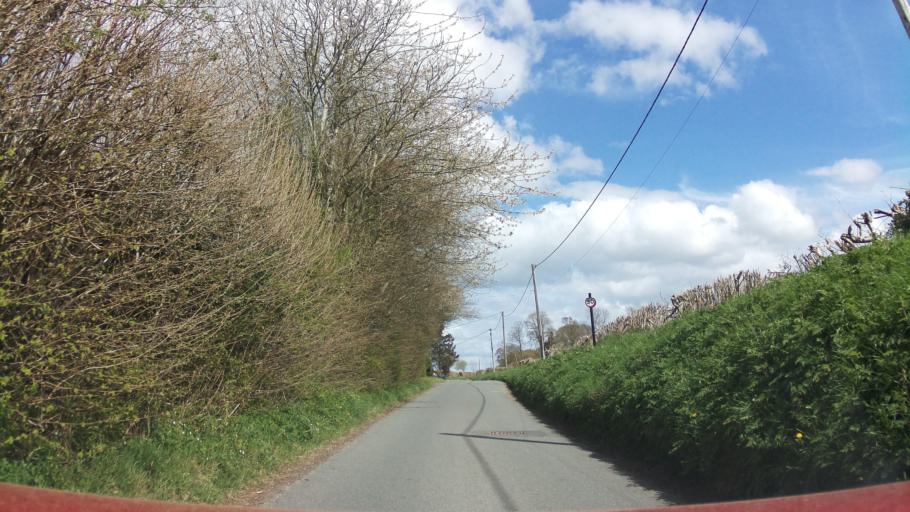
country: GB
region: England
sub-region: Wiltshire
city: Shalbourne
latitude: 51.3677
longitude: -1.5209
